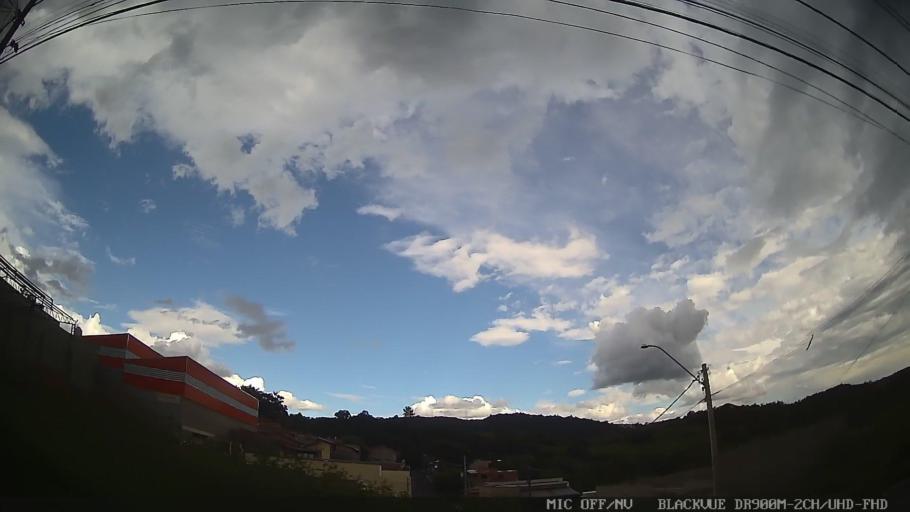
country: BR
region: Sao Paulo
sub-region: Pedreira
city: Pedreira
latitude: -22.7124
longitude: -46.8928
